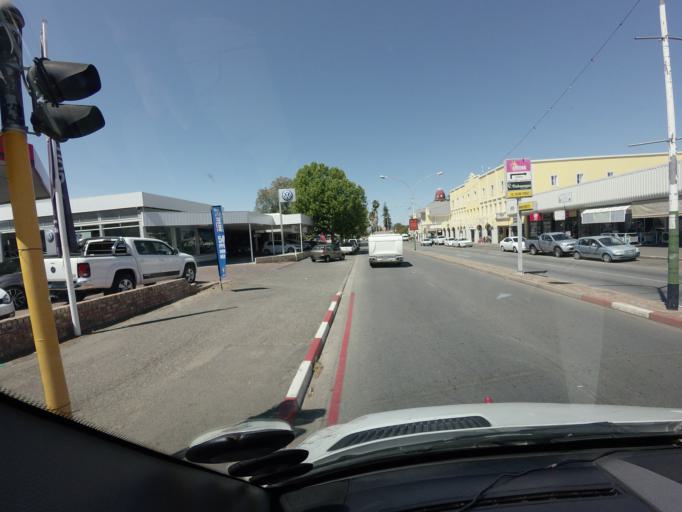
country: ZA
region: Western Cape
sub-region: Eden District Municipality
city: Oudtshoorn
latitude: -33.5907
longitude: 22.2030
